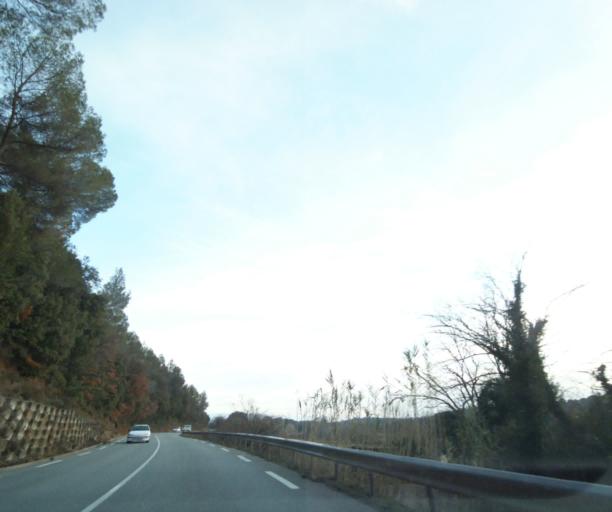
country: FR
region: Provence-Alpes-Cote d'Azur
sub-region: Departement du Var
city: Trans-en-Provence
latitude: 43.4951
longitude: 6.5101
